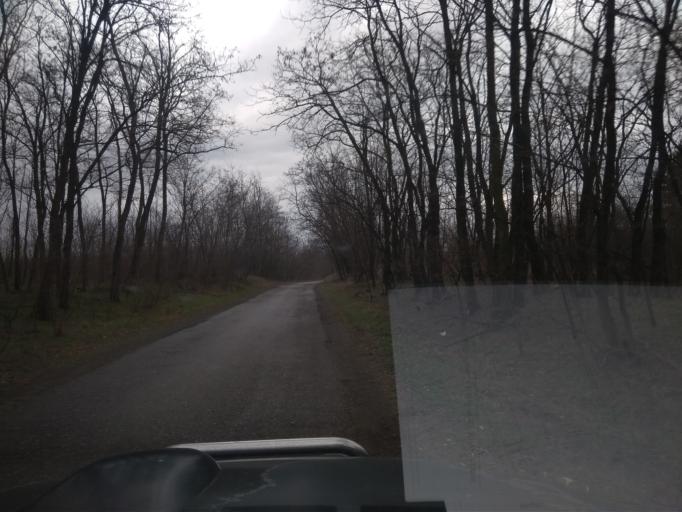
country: HU
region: Szabolcs-Szatmar-Bereg
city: Nyirpazony
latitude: 48.0213
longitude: 21.8056
